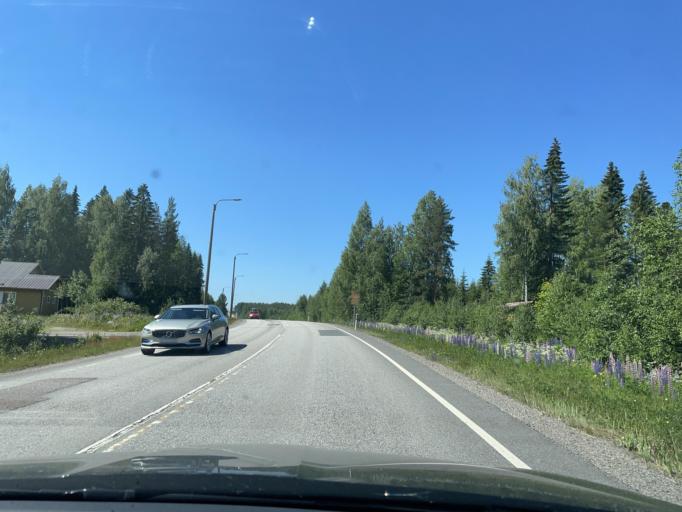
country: FI
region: Central Finland
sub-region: Saarijaervi-Viitasaari
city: Viitasaari
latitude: 63.1452
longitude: 25.8050
